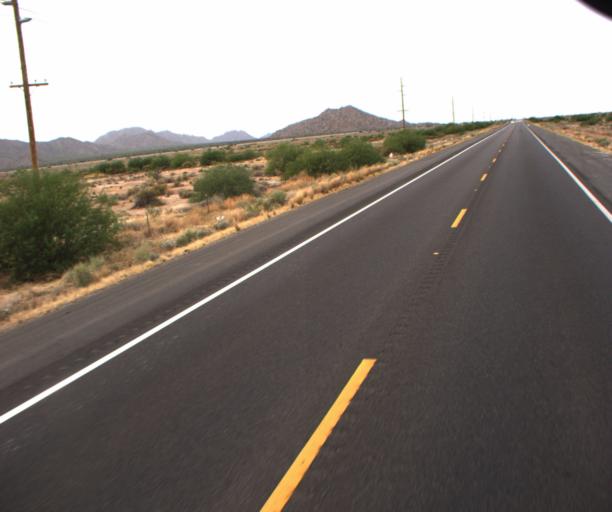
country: US
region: Arizona
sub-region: Pinal County
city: Blackwater
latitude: 33.0102
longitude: -111.6211
